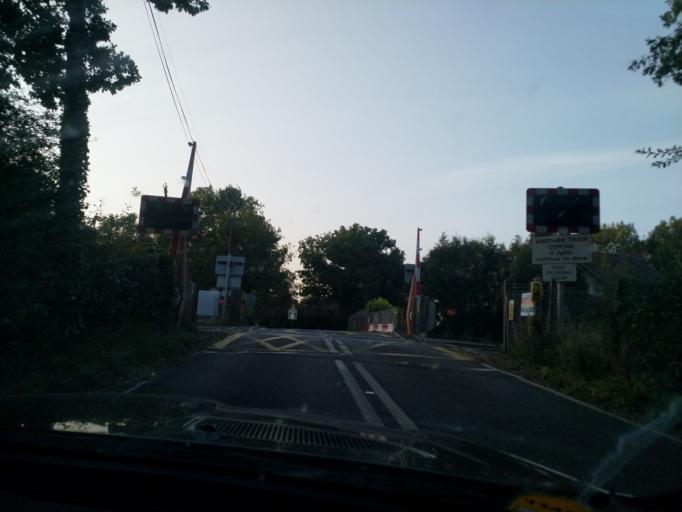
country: GB
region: England
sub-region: Kent
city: Sheerness
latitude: 51.4057
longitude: 0.8103
